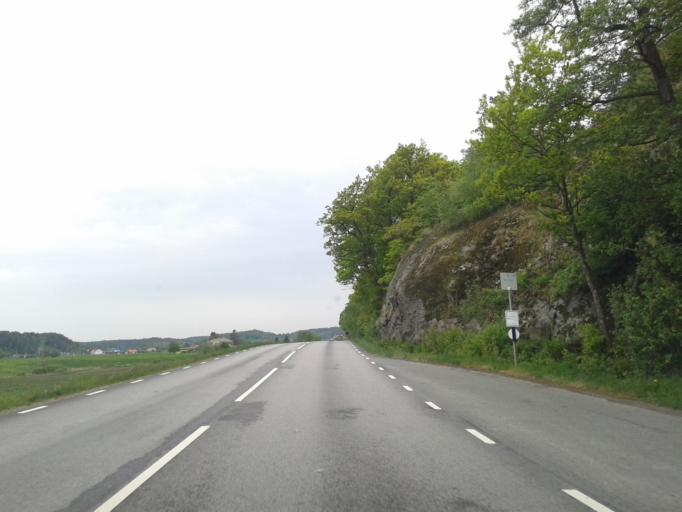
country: SE
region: Vaestra Goetaland
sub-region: Kungalvs Kommun
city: Kode
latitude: 57.8486
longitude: 11.8028
